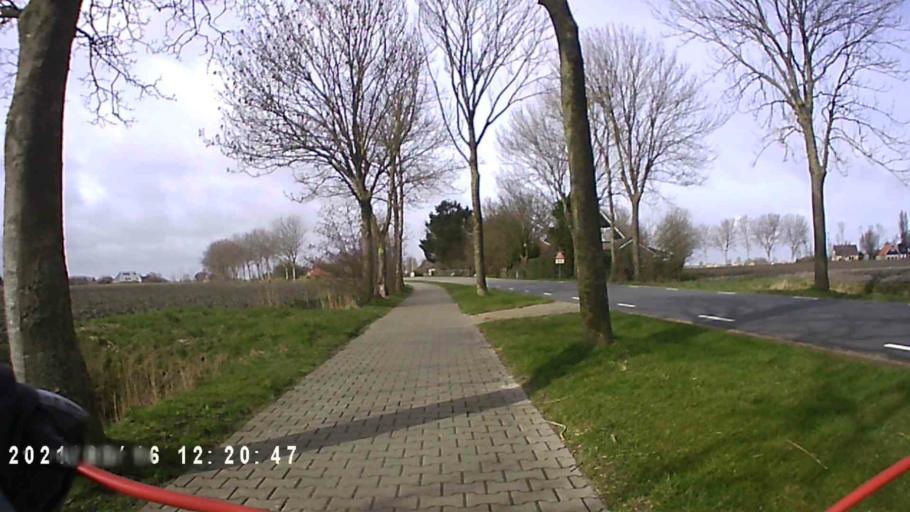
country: NL
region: Friesland
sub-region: Gemeente Ferwerderadiel
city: Hallum
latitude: 53.3075
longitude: 5.7654
